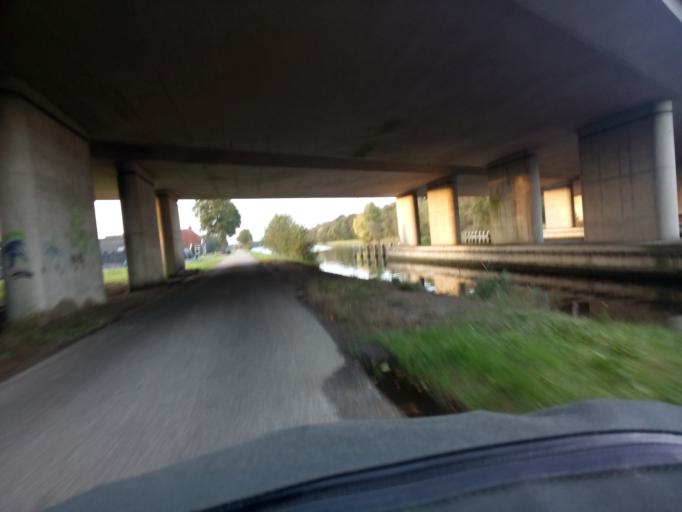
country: NL
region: Drenthe
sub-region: Gemeente Tynaarlo
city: Tynaarlo
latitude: 53.0613
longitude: 6.6017
